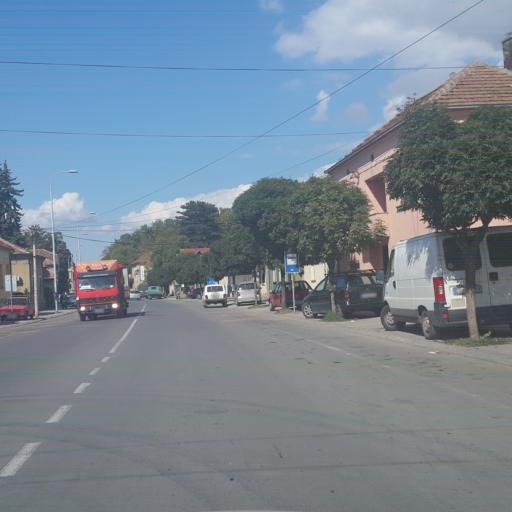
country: RS
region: Central Serbia
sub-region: Pirotski Okrug
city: Pirot
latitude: 43.1660
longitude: 22.5887
